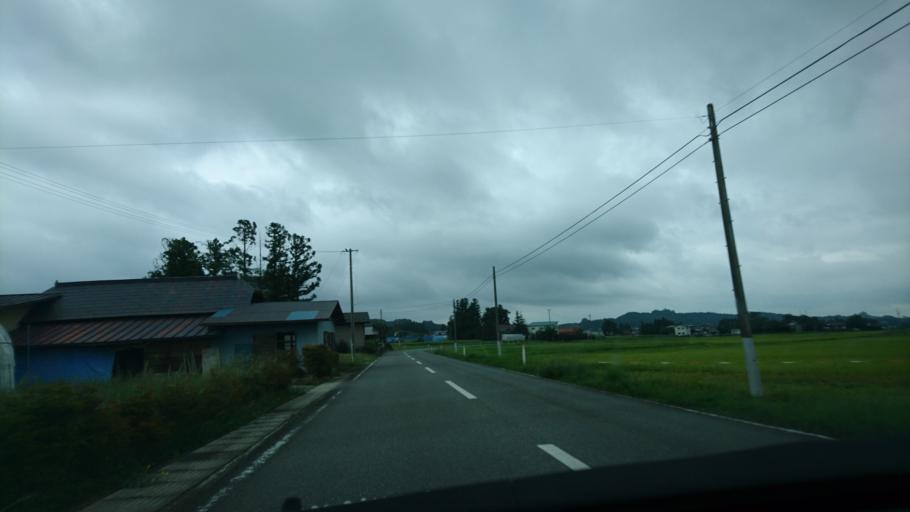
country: JP
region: Iwate
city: Ichinoseki
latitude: 38.8107
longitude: 140.9672
